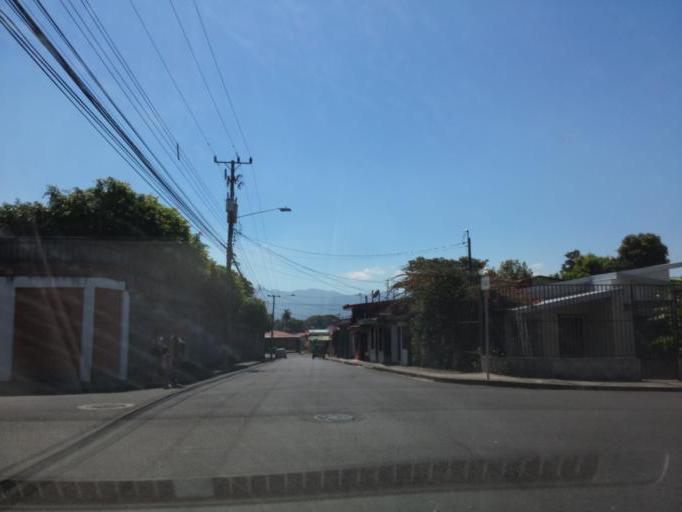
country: CR
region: Alajuela
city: Alajuela
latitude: 10.0139
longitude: -84.2091
